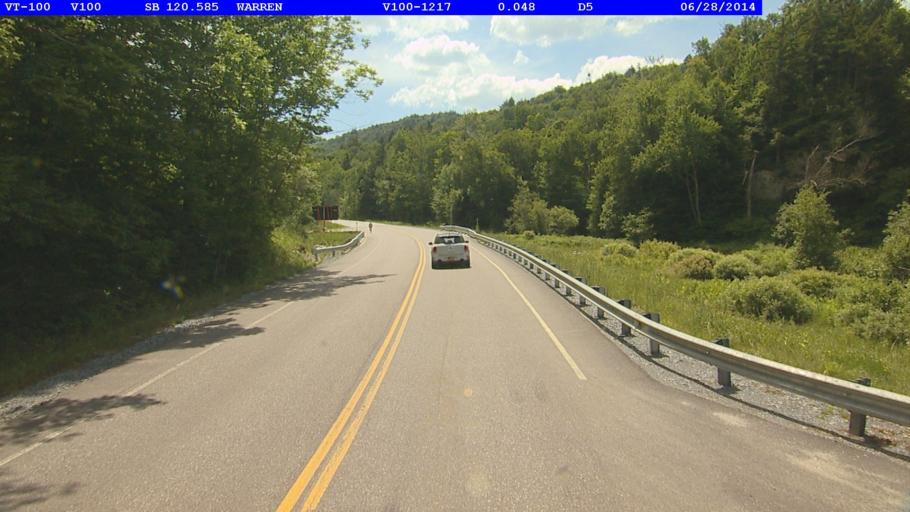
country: US
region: Vermont
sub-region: Washington County
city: Northfield
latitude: 44.0618
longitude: -72.8524
